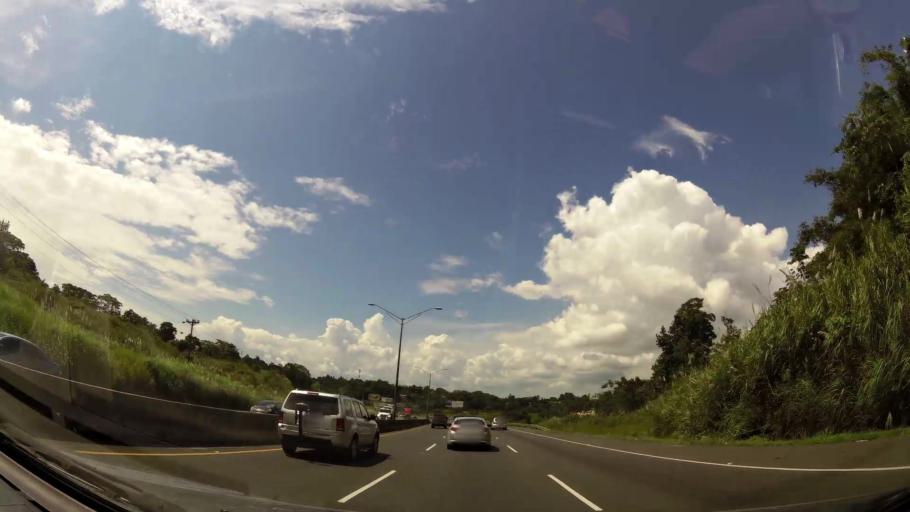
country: PA
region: Panama
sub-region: Distrito Arraijan
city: Arraijan
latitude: 8.9440
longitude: -79.6725
